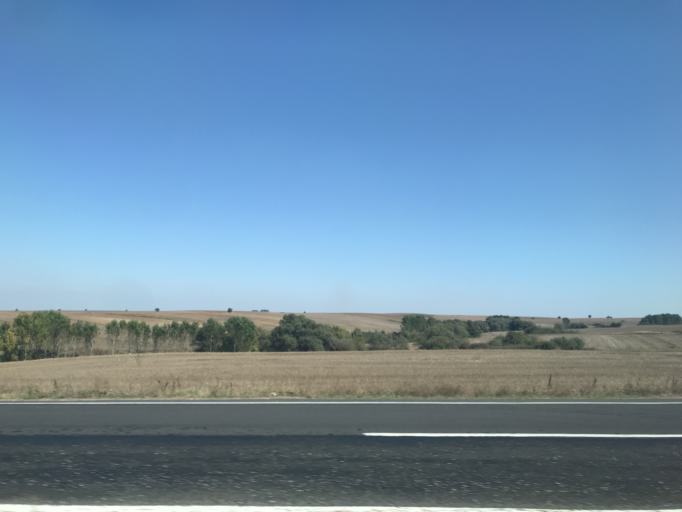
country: TR
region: Tekirdag
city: Muratli
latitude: 41.1169
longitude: 27.4900
